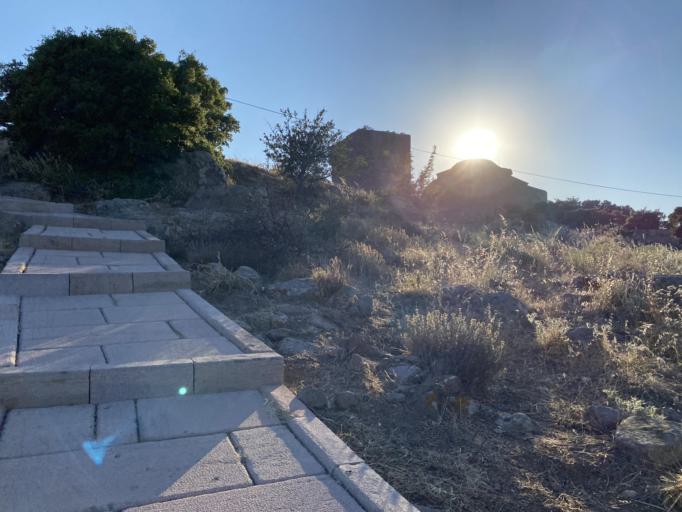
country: TR
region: Canakkale
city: Behram
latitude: 39.4917
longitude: 26.3379
